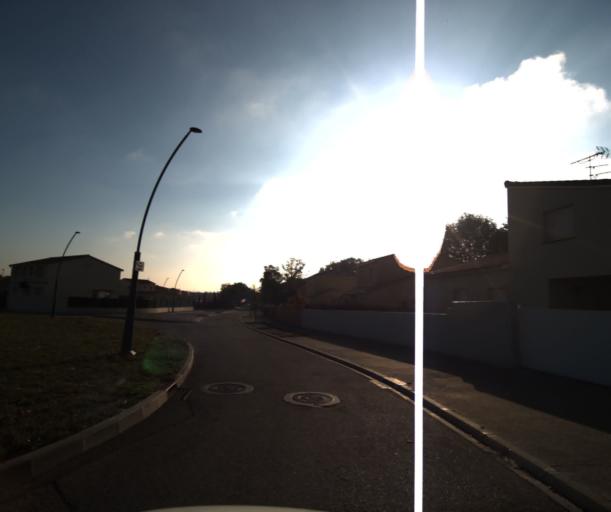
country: FR
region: Midi-Pyrenees
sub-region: Departement de la Haute-Garonne
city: Colomiers
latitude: 43.5939
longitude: 1.3412
